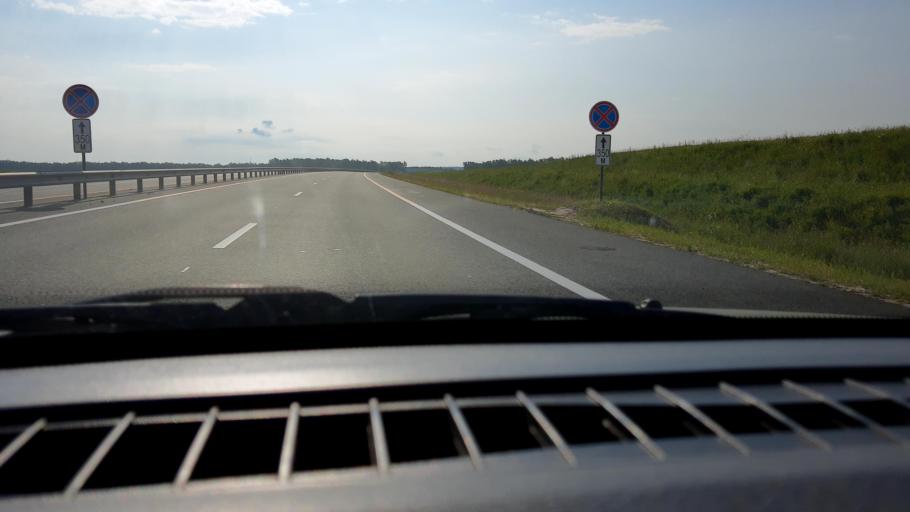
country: RU
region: Nizjnij Novgorod
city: Burevestnik
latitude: 56.1185
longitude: 43.9439
